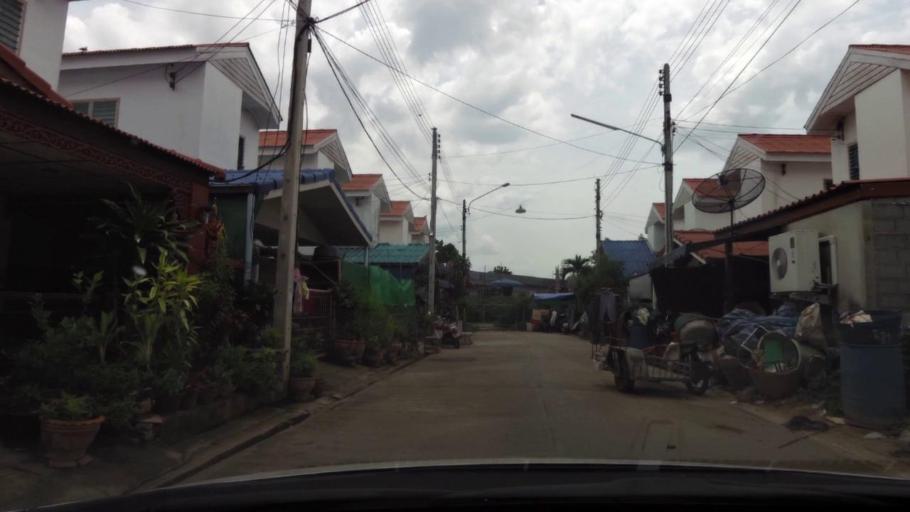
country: TH
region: Ratchaburi
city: Ratchaburi
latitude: 13.5365
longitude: 99.7914
